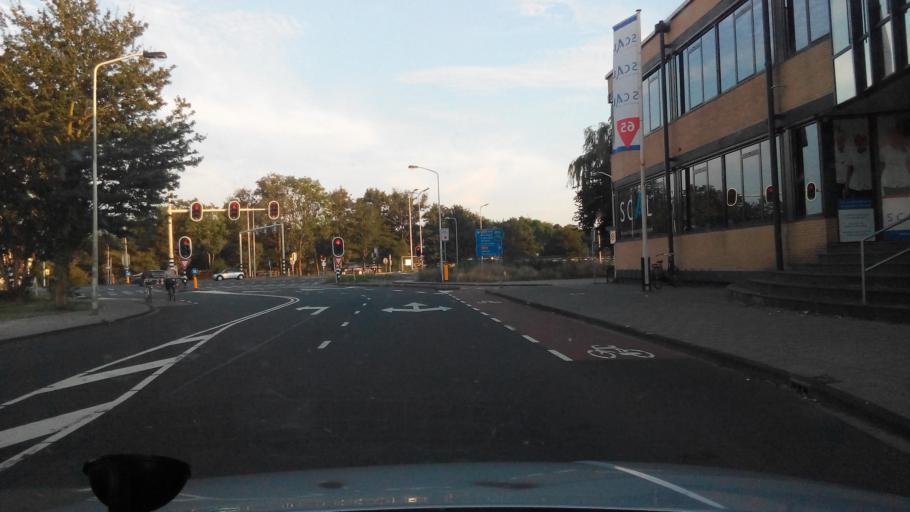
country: NL
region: South Holland
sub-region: Gemeente Leiden
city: Leiden
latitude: 52.1417
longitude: 4.4823
